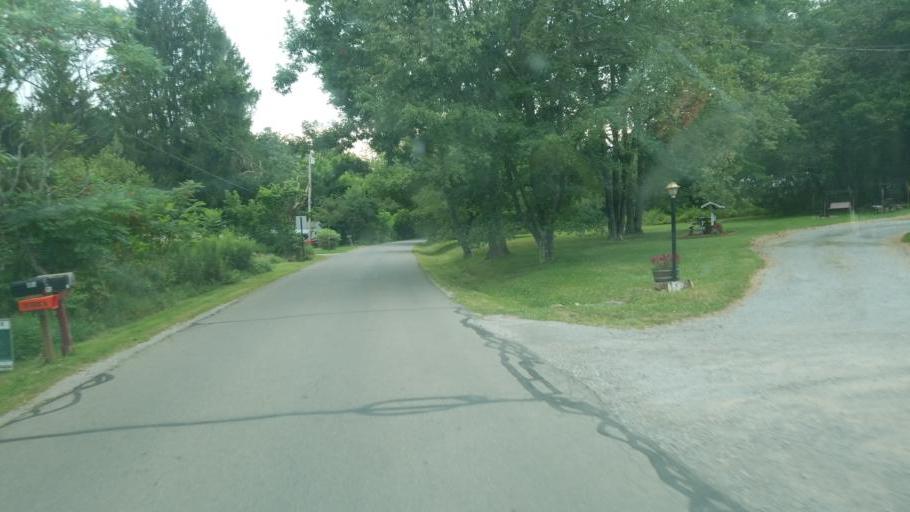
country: US
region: Pennsylvania
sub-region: Clarion County
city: Clarion
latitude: 41.2054
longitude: -79.3964
